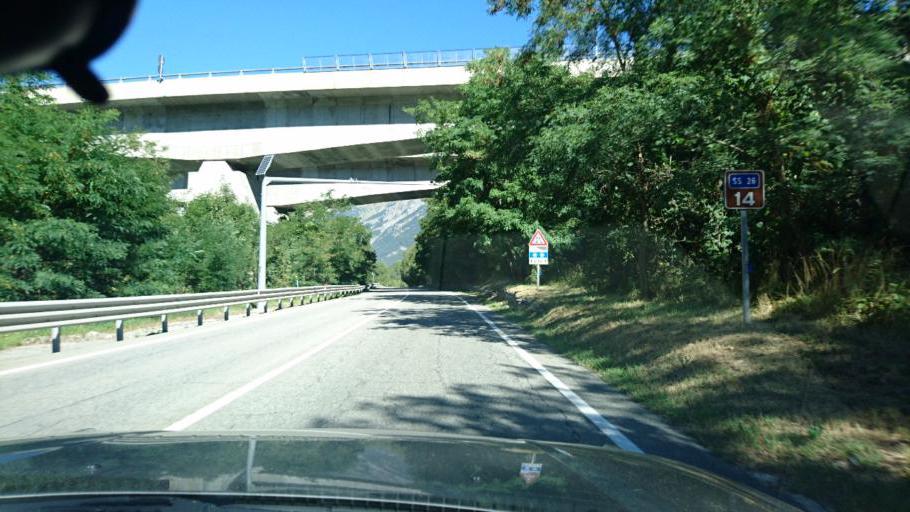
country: IT
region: Aosta Valley
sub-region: Valle d'Aosta
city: La Salle
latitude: 45.7362
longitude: 7.0715
